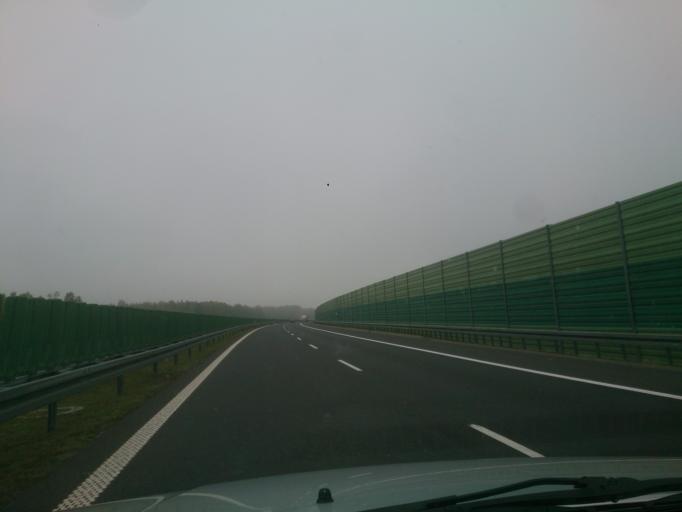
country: PL
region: Kujawsko-Pomorskie
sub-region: Powiat swiecki
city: Warlubie
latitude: 53.6560
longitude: 18.6385
